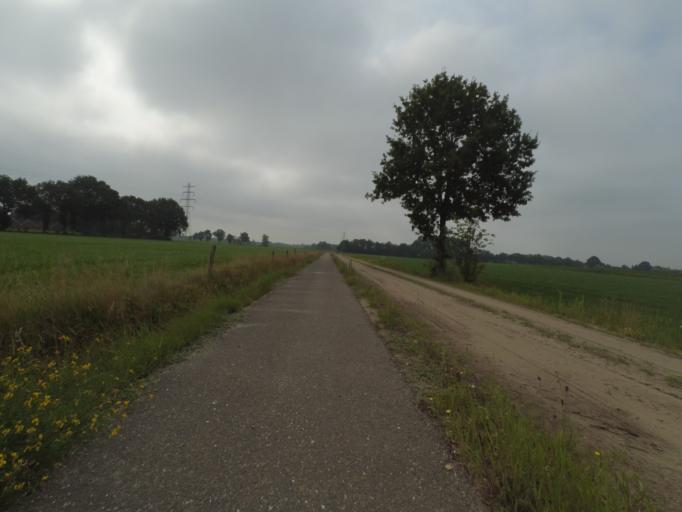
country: NL
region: Gelderland
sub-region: Gemeente Barneveld
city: Kootwijkerbroek
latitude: 52.1202
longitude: 5.6580
